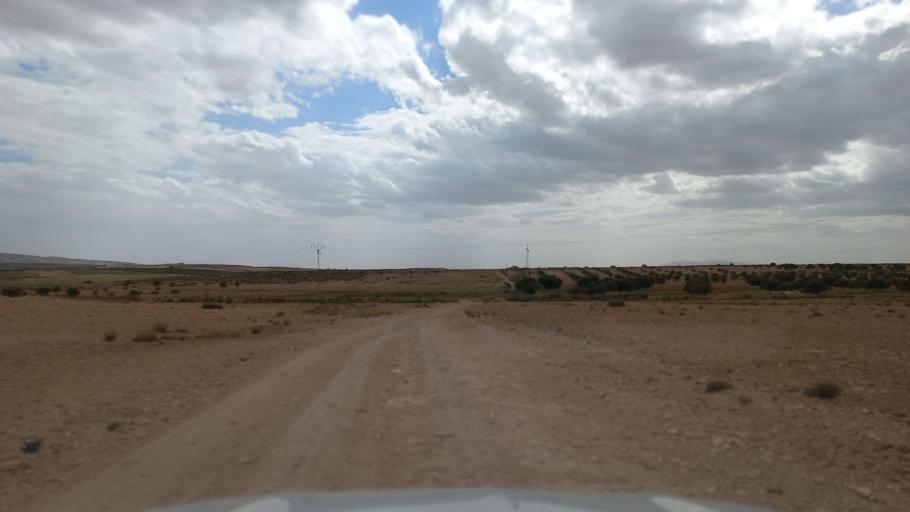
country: TN
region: Al Qasrayn
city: Sbiba
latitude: 35.3852
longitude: 9.1047
